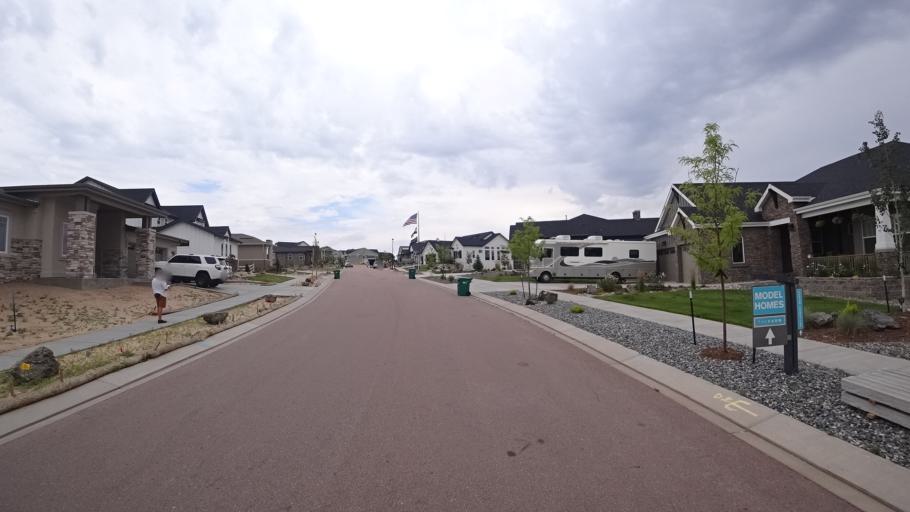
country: US
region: Colorado
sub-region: El Paso County
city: Gleneagle
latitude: 39.0034
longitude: -104.8084
